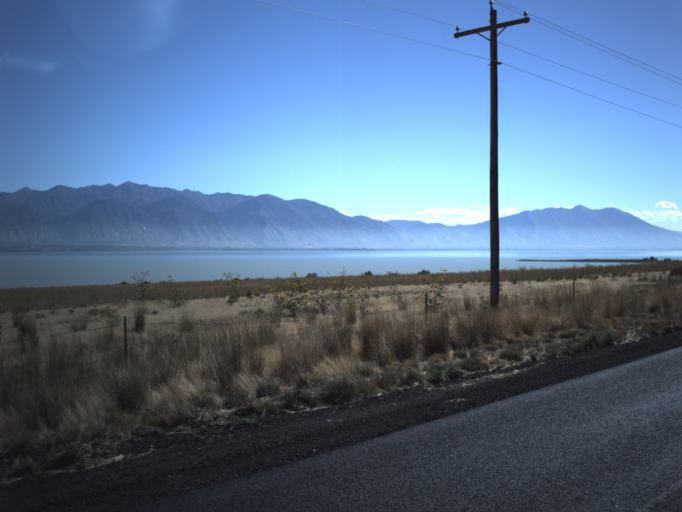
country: US
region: Utah
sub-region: Utah County
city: Saratoga Springs
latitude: 40.2794
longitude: -111.8704
